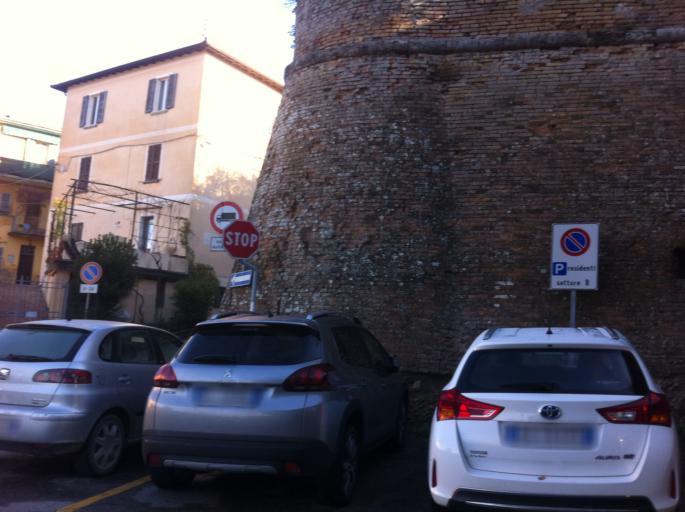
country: IT
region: Umbria
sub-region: Provincia di Perugia
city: Perugia
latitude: 43.1157
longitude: 12.3956
